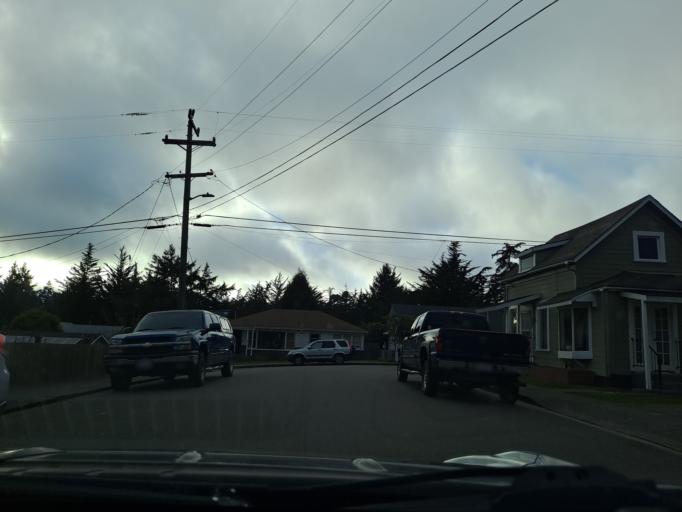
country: US
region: California
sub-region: Humboldt County
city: Fortuna
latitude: 40.6030
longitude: -124.1551
